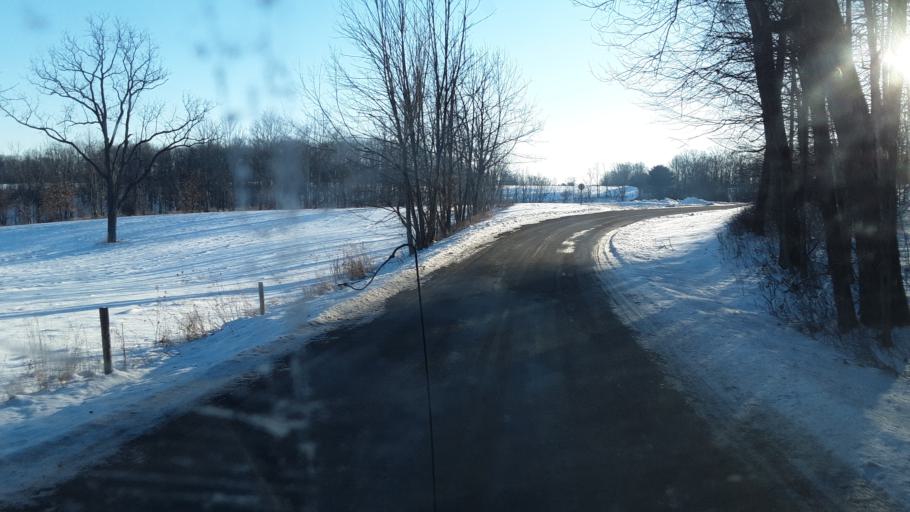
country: US
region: Ohio
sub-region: Knox County
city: Gambier
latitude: 40.2935
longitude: -82.3777
